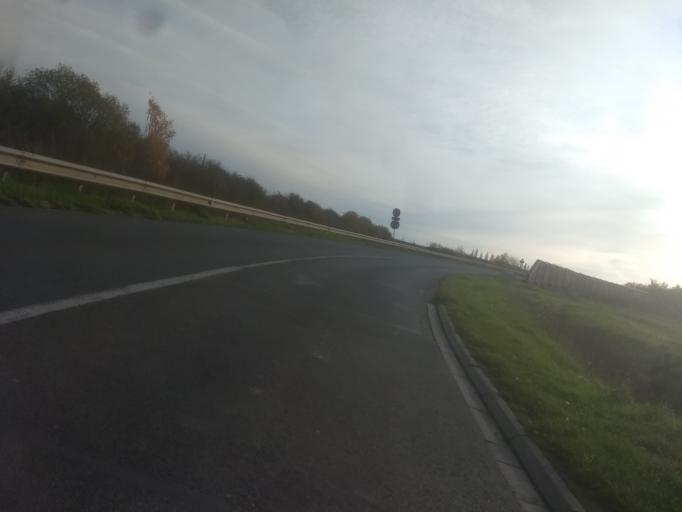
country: FR
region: Nord-Pas-de-Calais
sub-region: Departement du Pas-de-Calais
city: Agny
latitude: 50.2579
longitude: 2.7639
